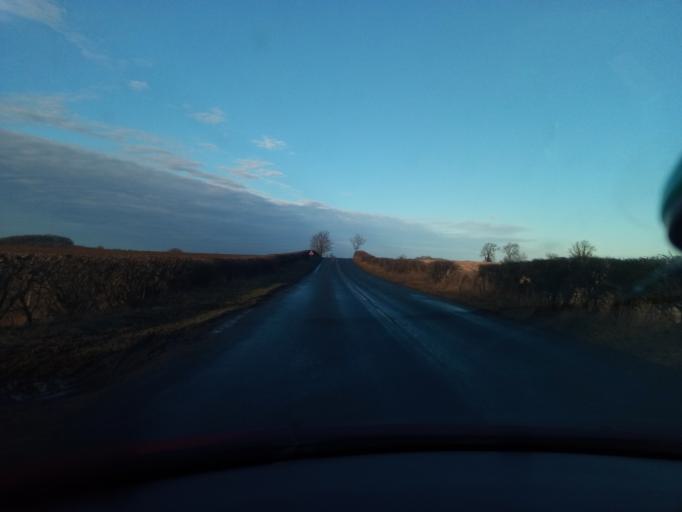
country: GB
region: England
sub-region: Darlington
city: High Coniscliffe
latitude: 54.4821
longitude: -1.6700
